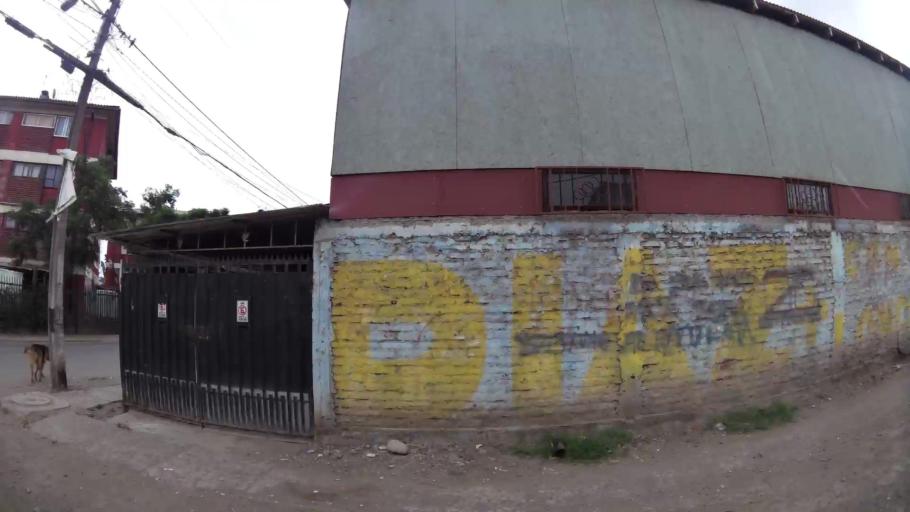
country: CL
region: Santiago Metropolitan
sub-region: Provincia de Maipo
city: San Bernardo
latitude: -33.5239
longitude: -70.6913
